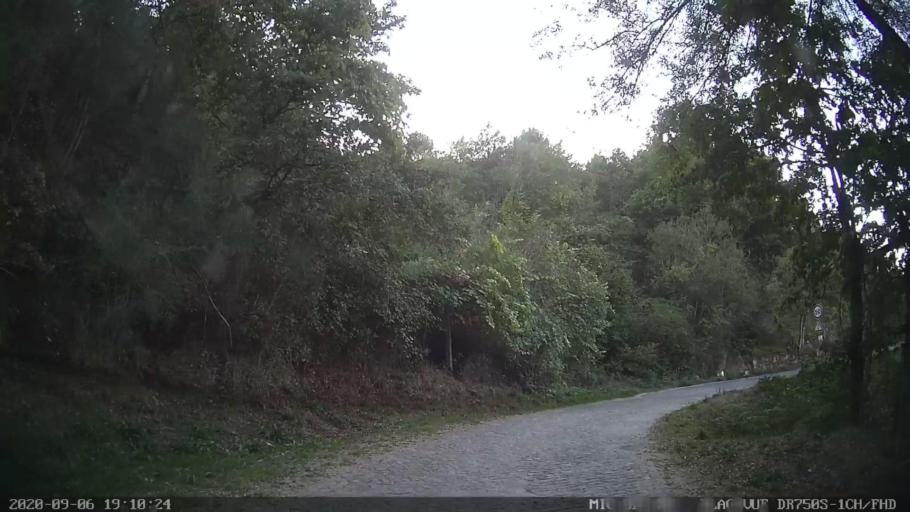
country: PT
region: Porto
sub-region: Baiao
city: Valadares
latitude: 41.2182
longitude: -7.9877
